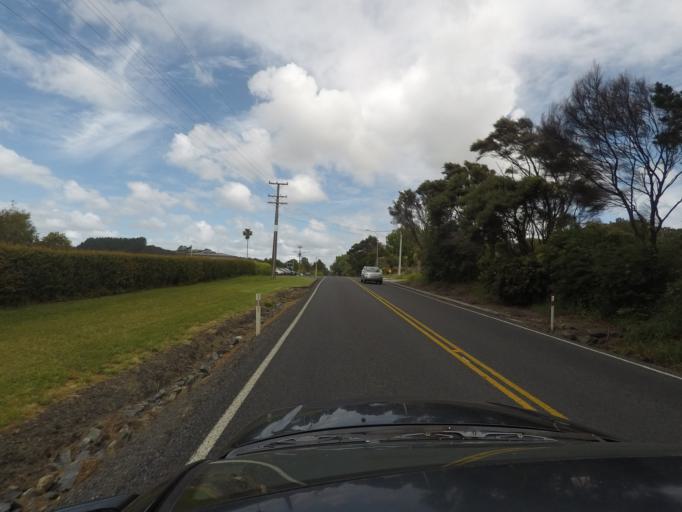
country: NZ
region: Auckland
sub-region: Auckland
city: Parakai
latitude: -36.6420
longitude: 174.5111
